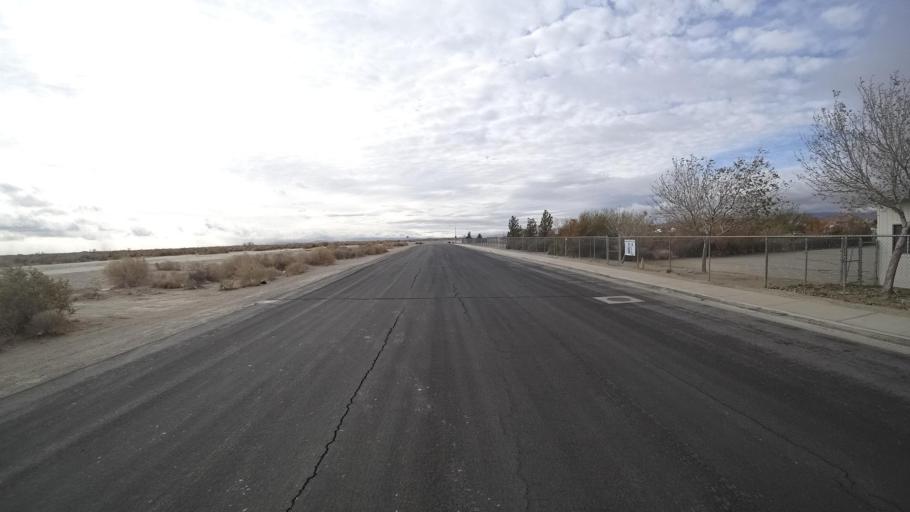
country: US
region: California
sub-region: Kern County
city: Rosamond
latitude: 34.8493
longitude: -118.1961
